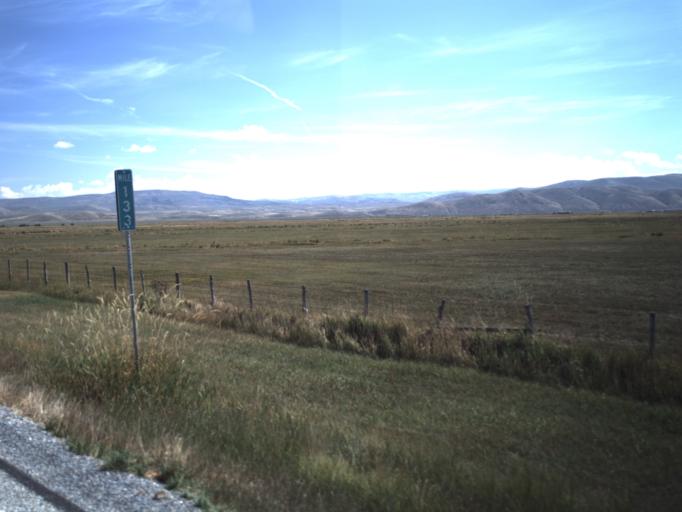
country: US
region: Utah
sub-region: Rich County
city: Randolph
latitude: 41.7749
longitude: -111.0969
